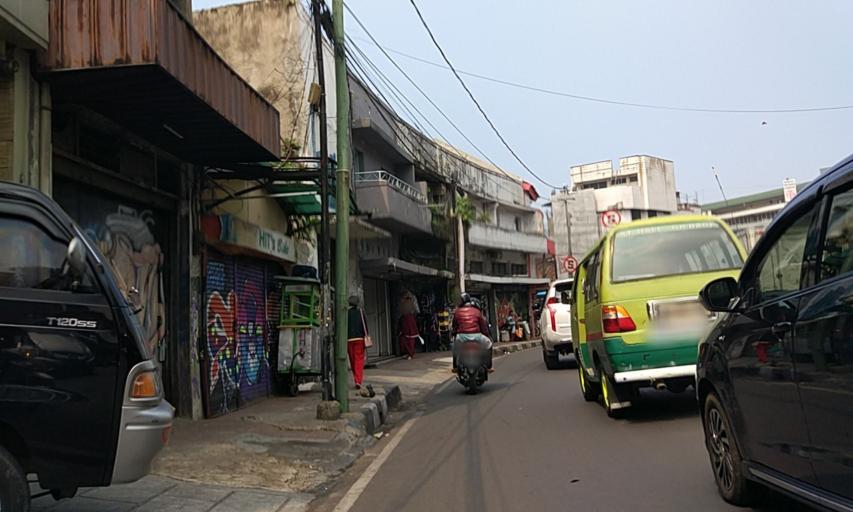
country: ID
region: West Java
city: Bandung
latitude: -6.9210
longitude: 107.6191
